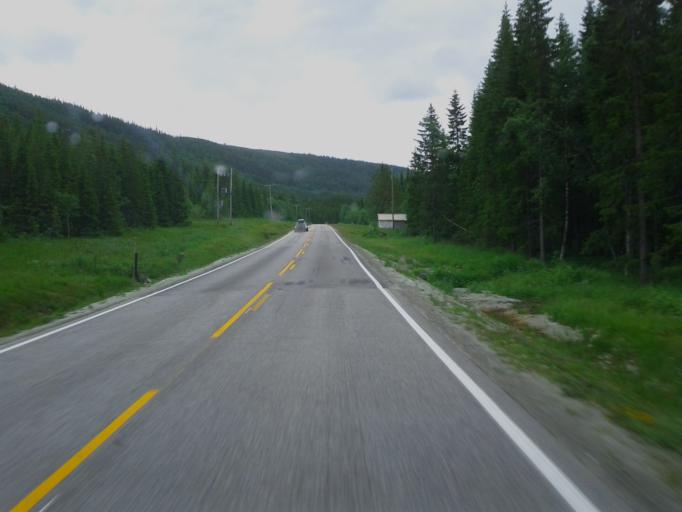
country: NO
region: Nord-Trondelag
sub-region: Namsskogan
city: Namsskogan
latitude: 64.8777
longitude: 13.0670
